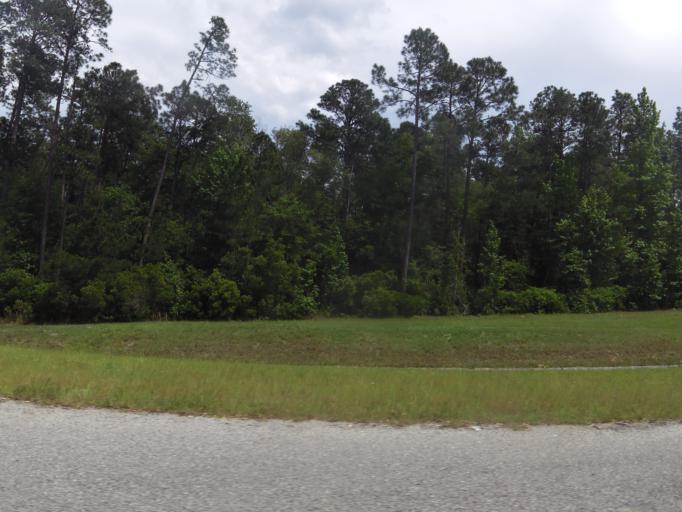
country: US
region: Georgia
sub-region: Emanuel County
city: Swainsboro
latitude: 32.6230
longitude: -82.3757
